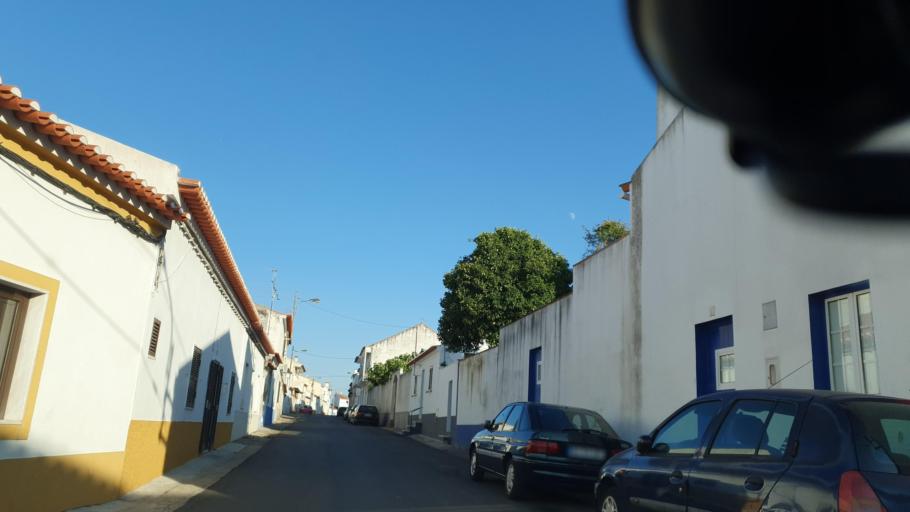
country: PT
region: Portalegre
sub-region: Fronteira
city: Fronteira
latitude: 38.9564
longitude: -7.6765
